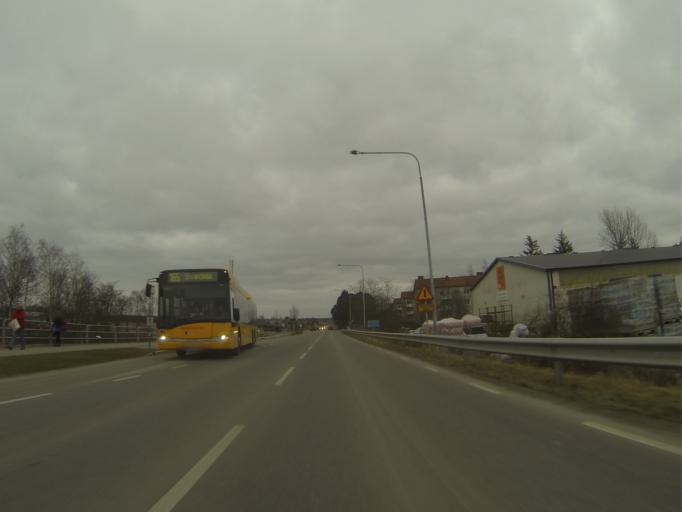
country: SE
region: Skane
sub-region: Svedala Kommun
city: Svedala
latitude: 55.5157
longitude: 13.2365
